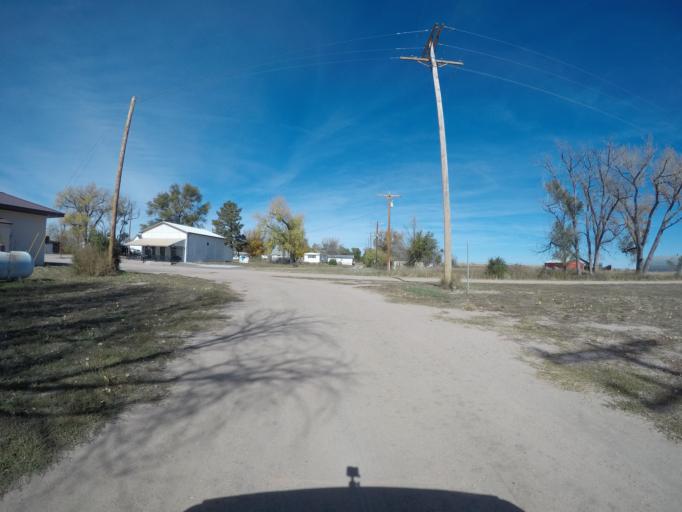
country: US
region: Colorado
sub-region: Yuma County
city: Yuma
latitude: 39.6623
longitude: -102.8503
